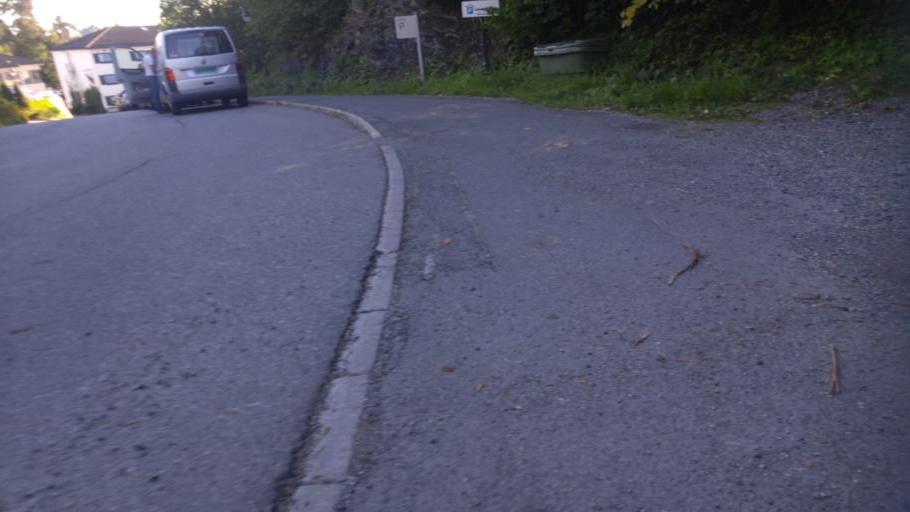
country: NO
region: Akershus
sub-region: Asker
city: Billingstad
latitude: 59.8510
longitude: 10.4932
